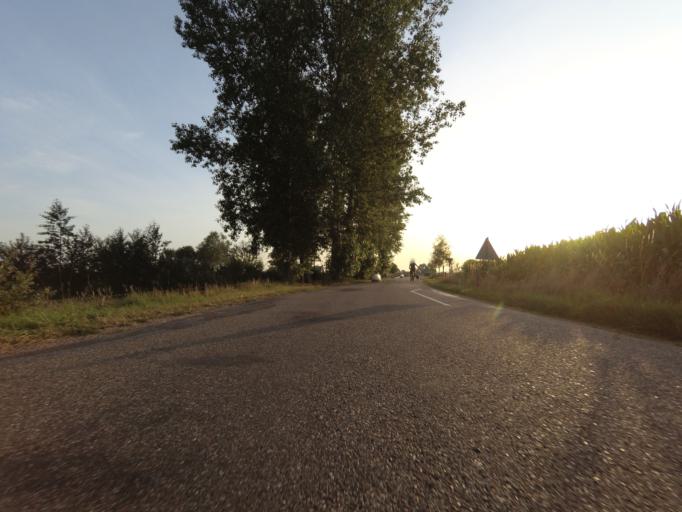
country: NL
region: Overijssel
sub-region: Gemeente Wierden
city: Wierden
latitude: 52.3313
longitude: 6.5102
